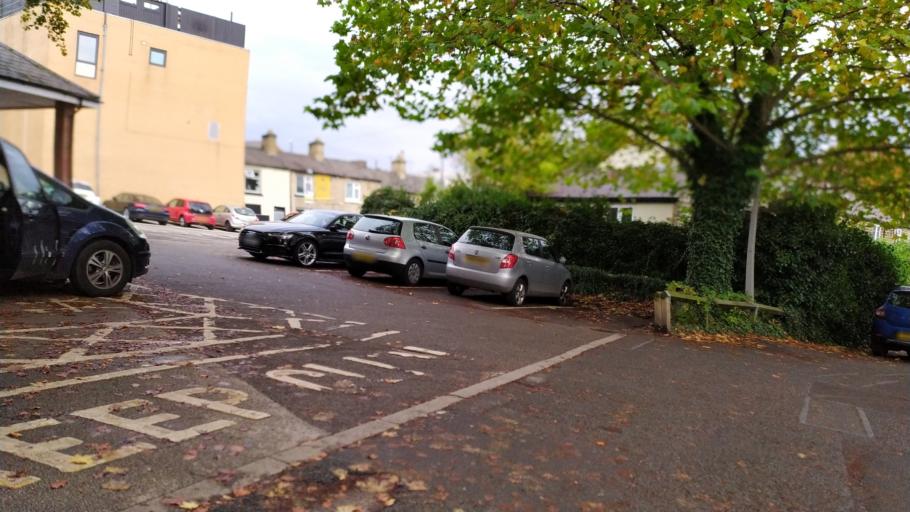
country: GB
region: England
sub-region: City and Borough of Leeds
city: Chapel Allerton
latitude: 53.8283
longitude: -1.5388
